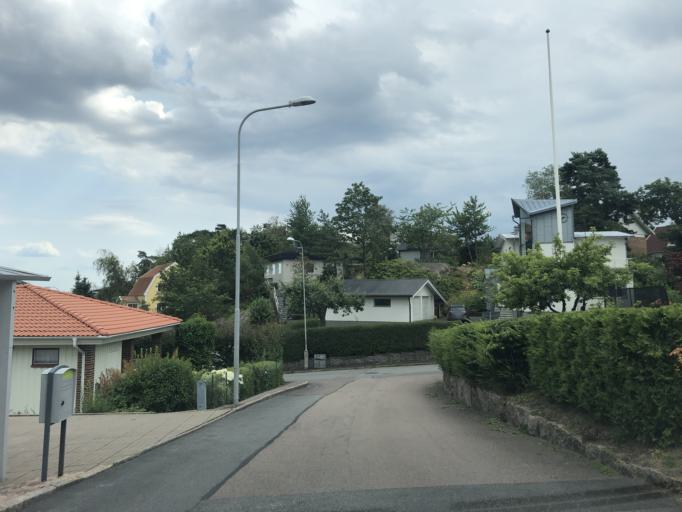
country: SE
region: Vaestra Goetaland
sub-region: Goteborg
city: Majorna
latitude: 57.7368
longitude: 11.9082
